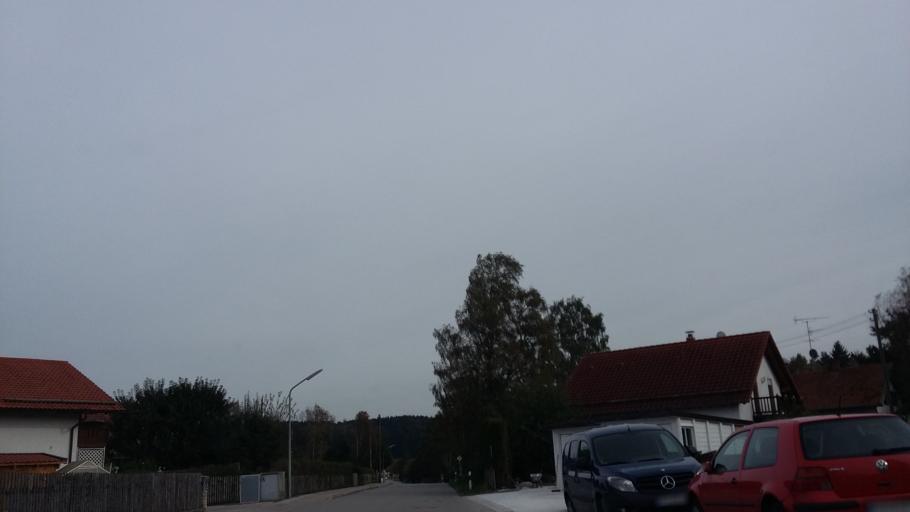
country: DE
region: Bavaria
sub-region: Upper Bavaria
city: Munsing
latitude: 47.9314
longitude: 11.3880
